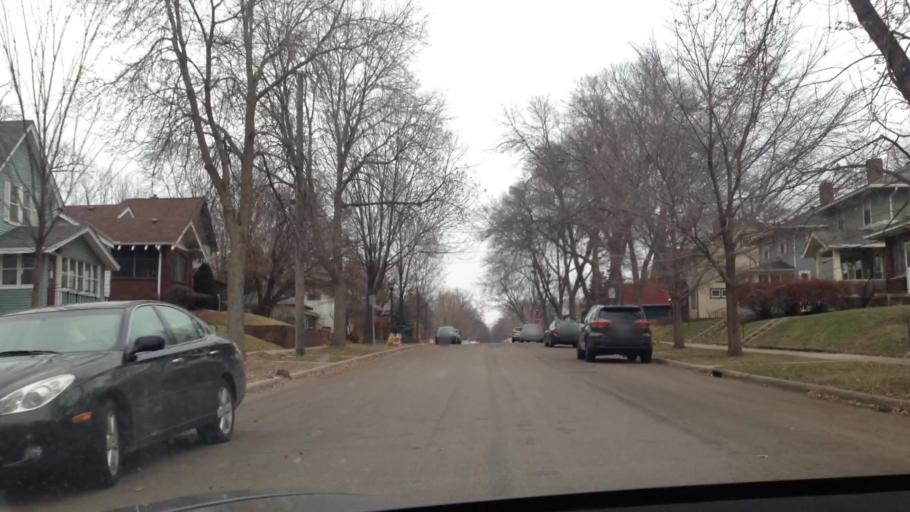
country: US
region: Minnesota
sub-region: Ramsey County
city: Falcon Heights
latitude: 44.9380
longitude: -93.1890
